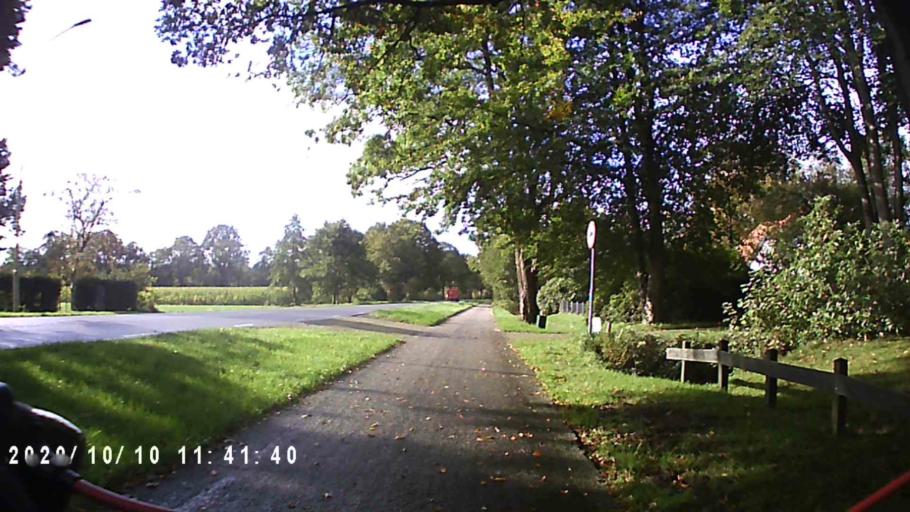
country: NL
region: Friesland
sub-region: Gemeente Smallingerland
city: Drachten
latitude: 53.0641
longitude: 6.1005
